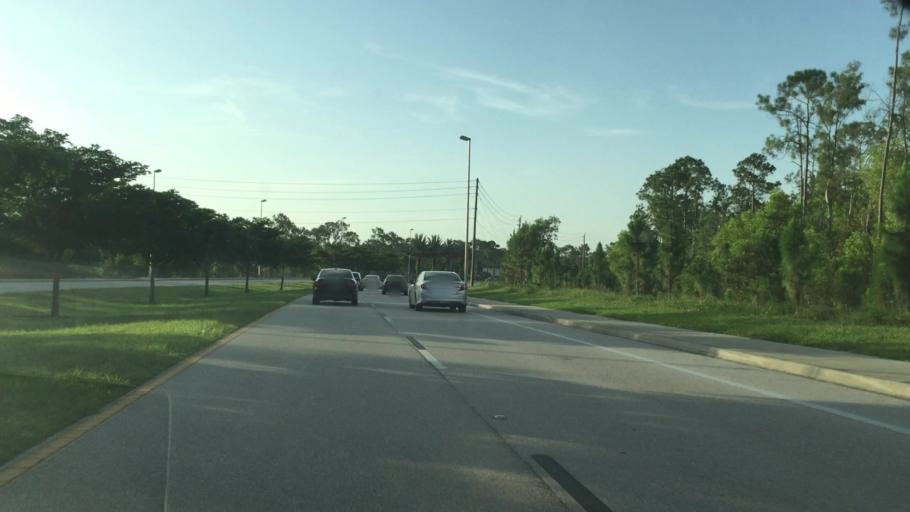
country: US
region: Florida
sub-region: Lee County
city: Three Oaks
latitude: 26.4666
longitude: -81.7915
